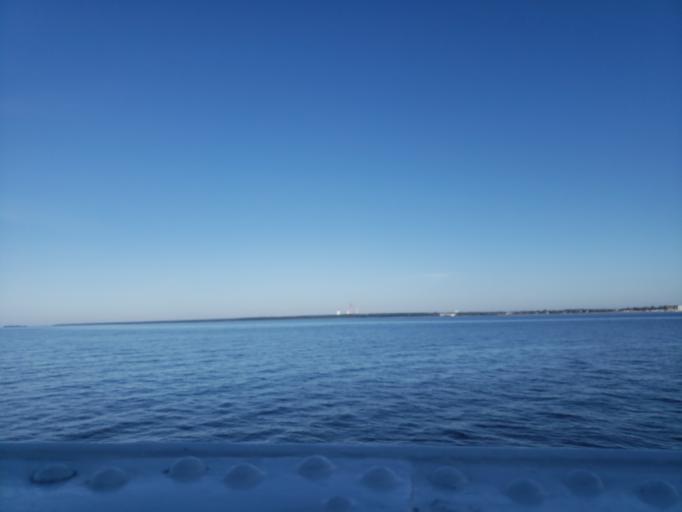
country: RU
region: St.-Petersburg
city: Lakhtinskiy
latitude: 59.9586
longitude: 30.1697
